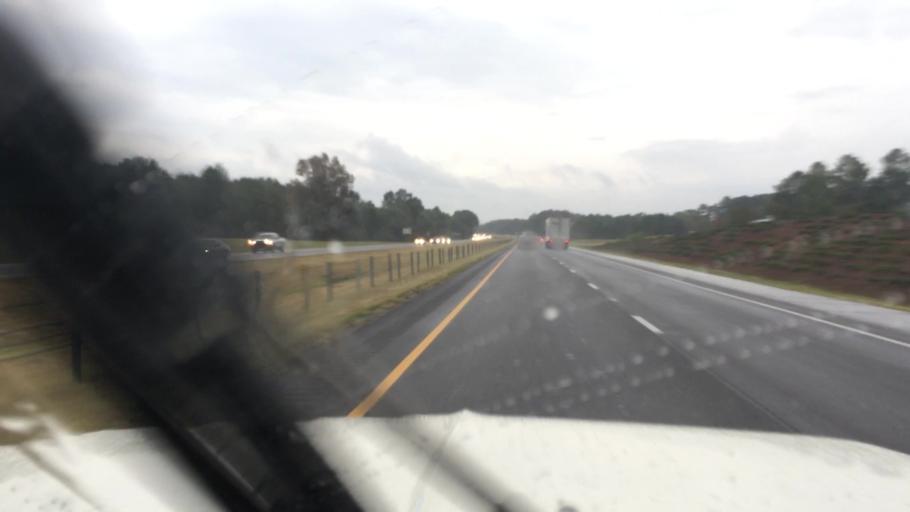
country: US
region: Alabama
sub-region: Morgan County
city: Falkville
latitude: 34.4120
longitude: -86.8985
